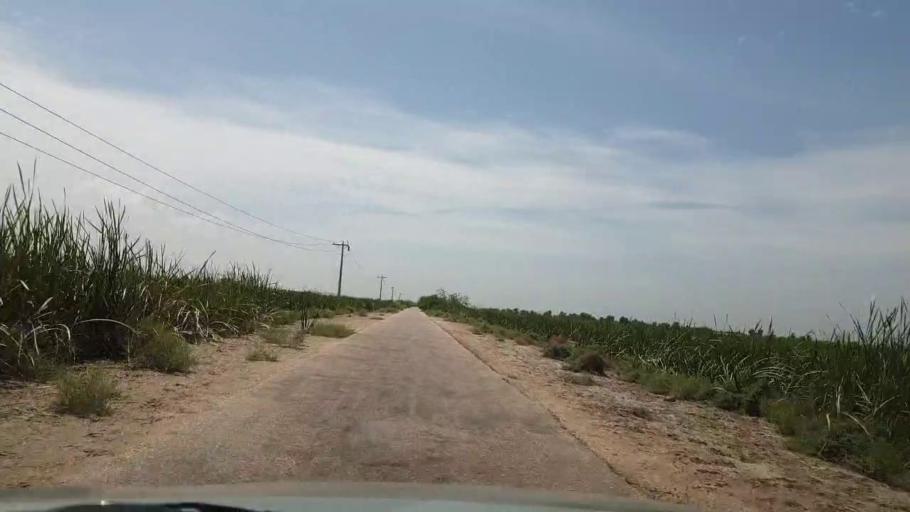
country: PK
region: Sindh
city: Bozdar
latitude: 27.0640
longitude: 68.9825
